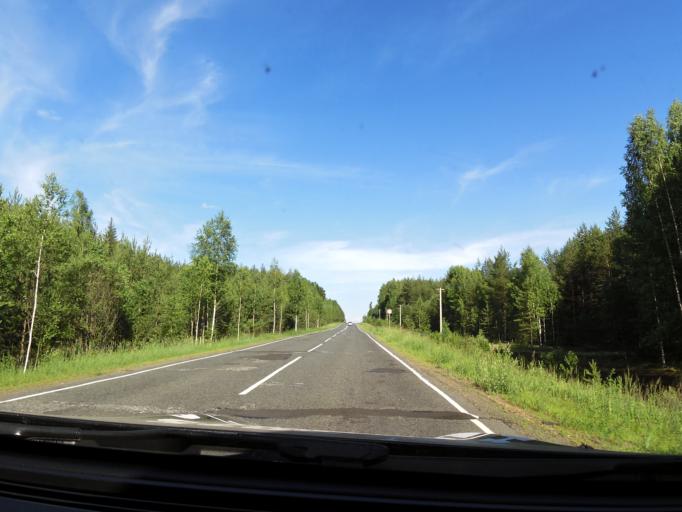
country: RU
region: Kirov
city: Belaya Kholunitsa
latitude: 58.9063
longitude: 51.0200
